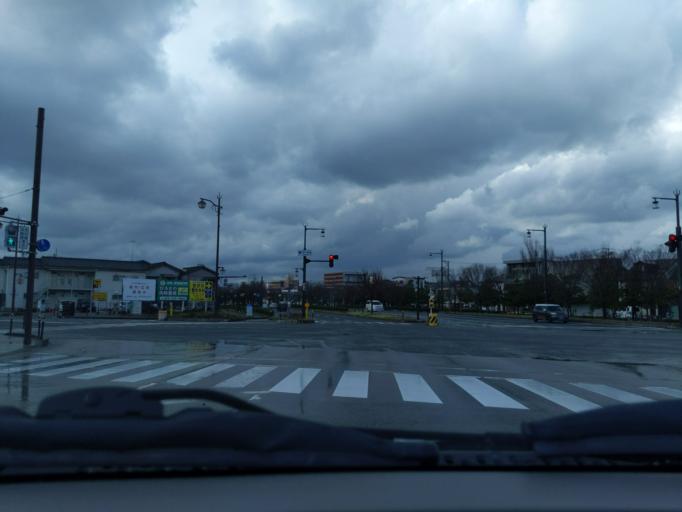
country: JP
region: Niigata
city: Niigata-shi
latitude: 37.9249
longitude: 139.0528
